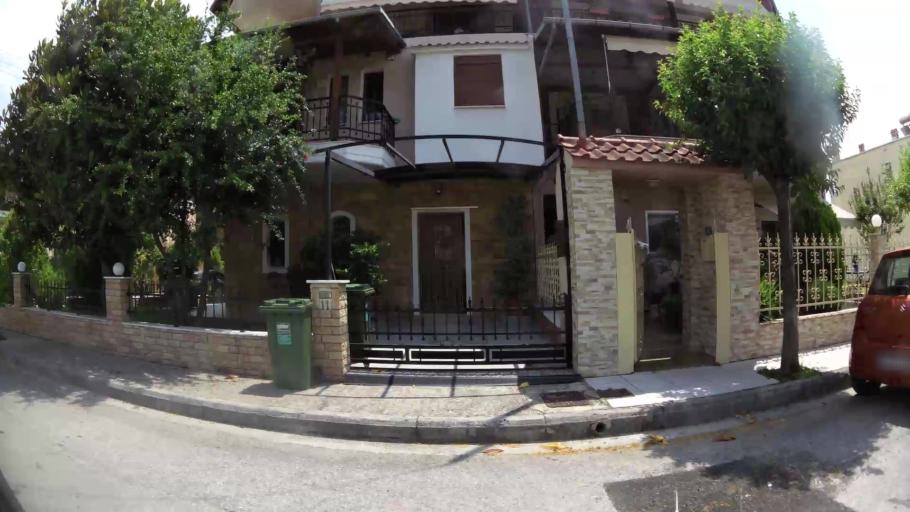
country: GR
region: Central Macedonia
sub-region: Nomos Pierias
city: Katerini
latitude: 40.2642
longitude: 22.5175
